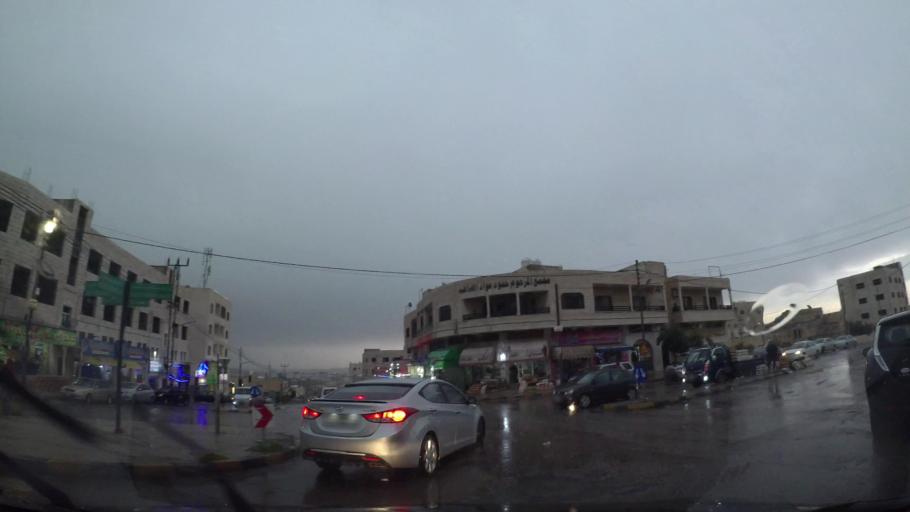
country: JO
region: Amman
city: Amman
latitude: 32.0018
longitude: 35.9689
